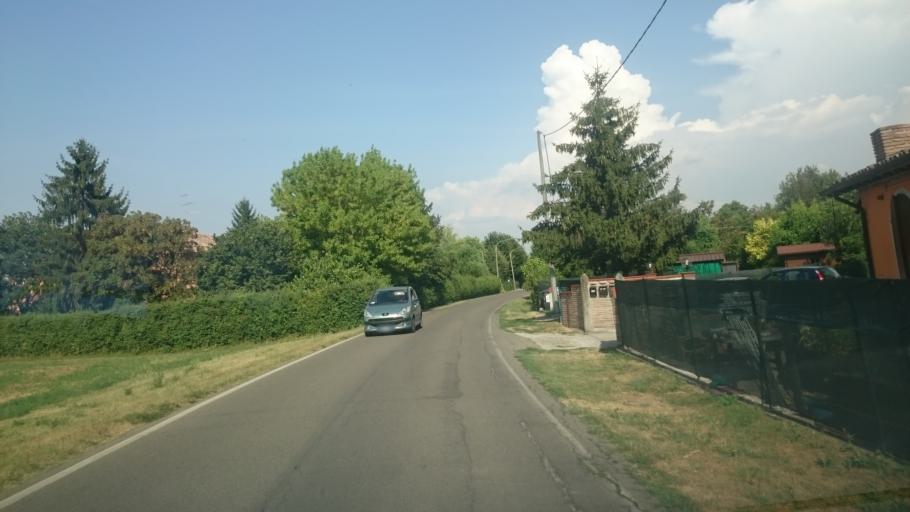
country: IT
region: Emilia-Romagna
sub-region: Provincia di Reggio Emilia
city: Bagno
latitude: 44.6482
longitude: 10.7578
